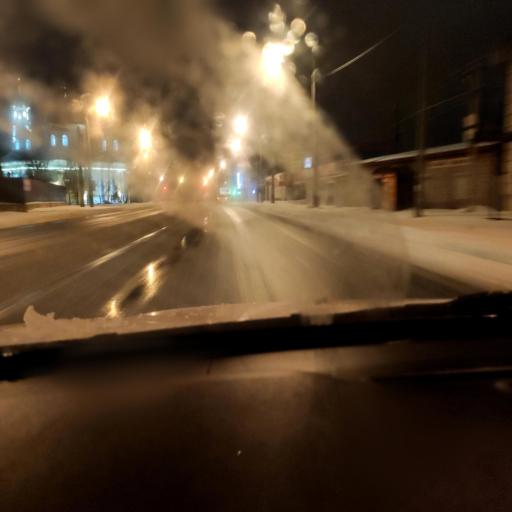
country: RU
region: Samara
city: Volzhskiy
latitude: 53.4249
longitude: 50.1237
